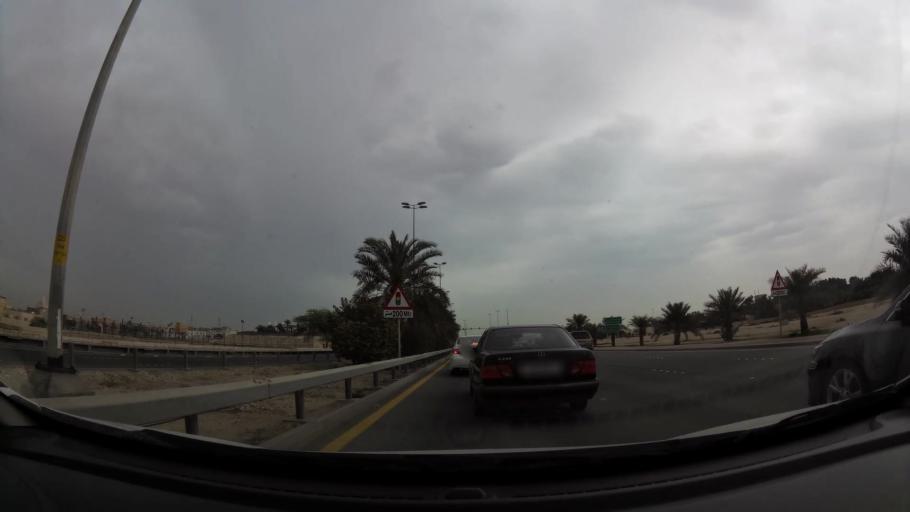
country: BH
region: Central Governorate
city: Dar Kulayb
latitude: 26.0578
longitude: 50.5066
